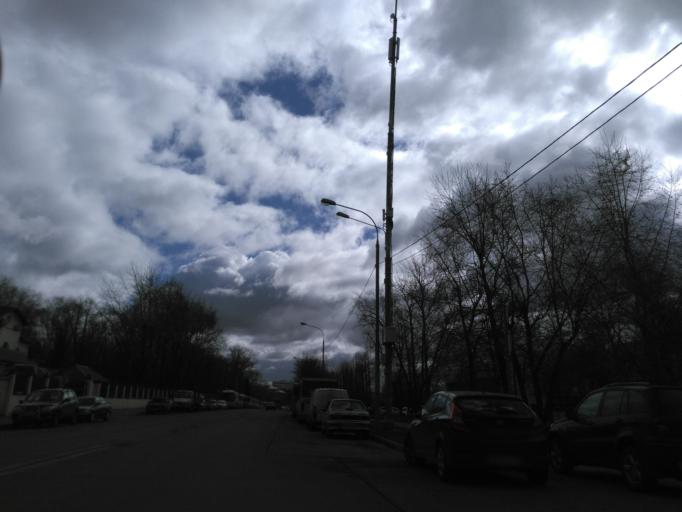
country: RU
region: Moscow
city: Golovinskiy
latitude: 55.8392
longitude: 37.4942
